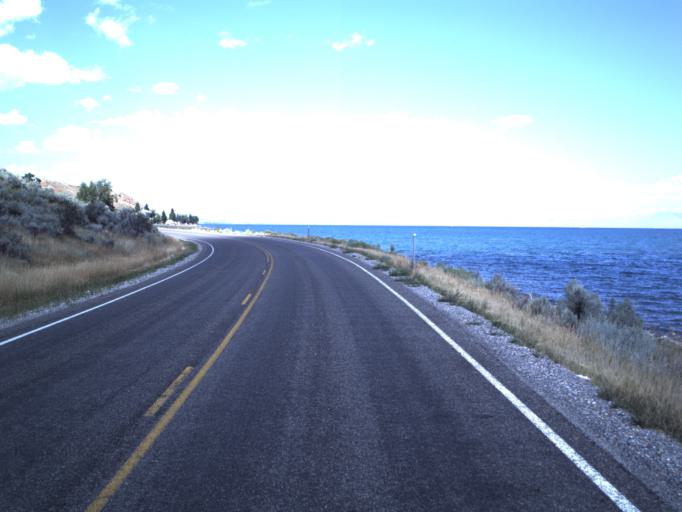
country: US
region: Utah
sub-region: Rich County
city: Randolph
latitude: 41.8955
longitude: -111.3664
